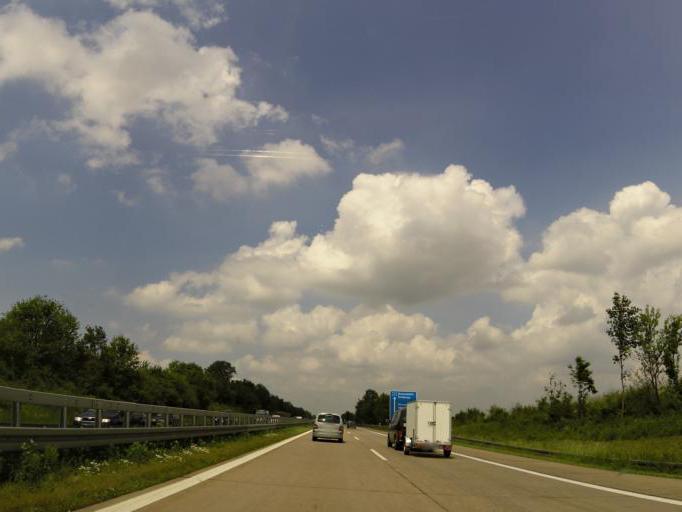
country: DE
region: Baden-Wuerttemberg
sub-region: Regierungsbezirk Stuttgart
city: Ellwangen
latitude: 48.9496
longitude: 10.1884
